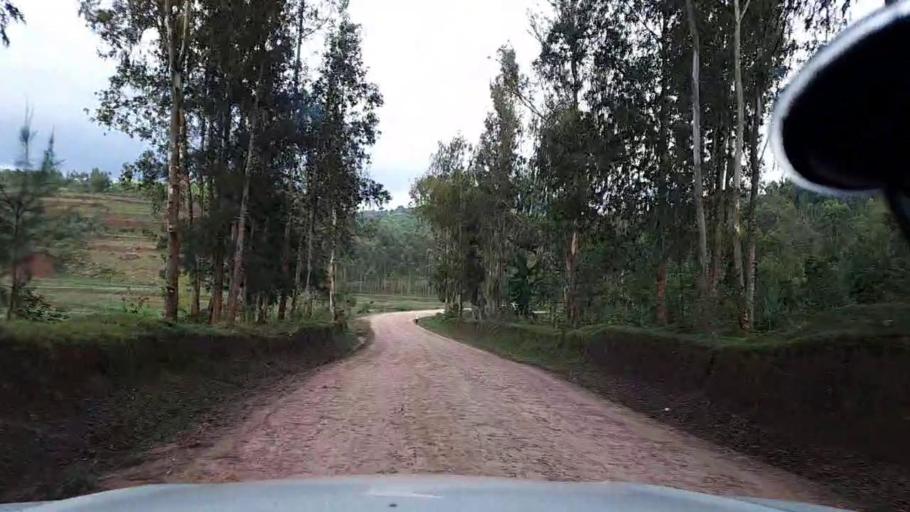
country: RW
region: Southern Province
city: Gitarama
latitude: -2.2095
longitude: 29.6154
